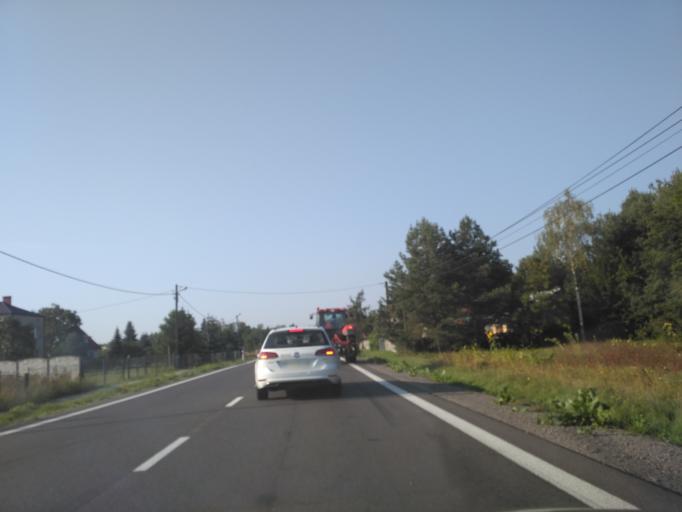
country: PL
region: Subcarpathian Voivodeship
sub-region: Powiat nizanski
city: Nisko
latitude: 50.5034
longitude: 22.1405
